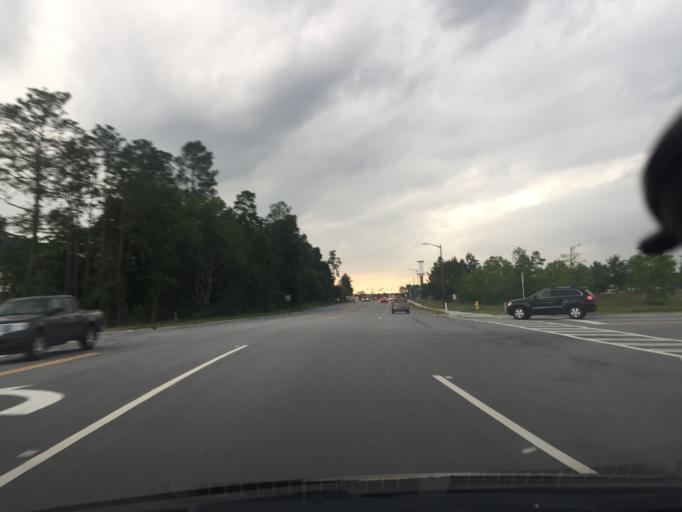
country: US
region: Georgia
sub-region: Chatham County
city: Pooler
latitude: 32.1372
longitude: -81.2467
